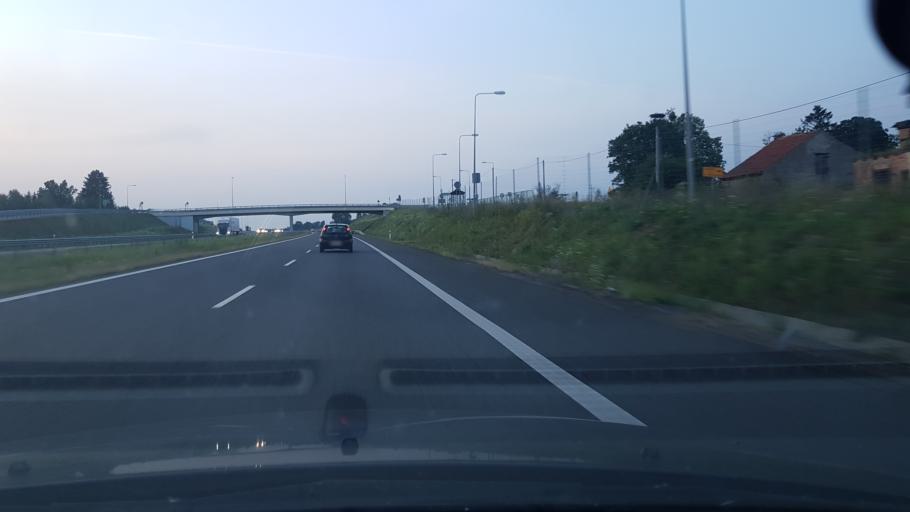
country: PL
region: Warmian-Masurian Voivodeship
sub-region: Powiat olsztynski
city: Olsztynek
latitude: 53.4755
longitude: 20.3209
